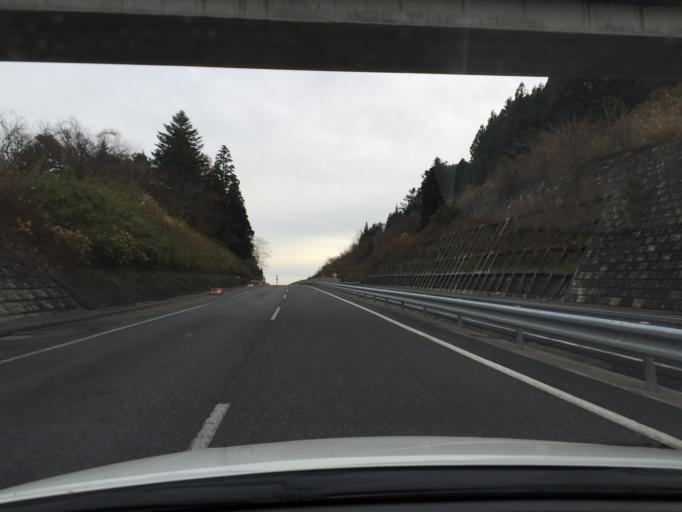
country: JP
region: Fukushima
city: Funehikimachi-funehiki
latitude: 37.2769
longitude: 140.6227
